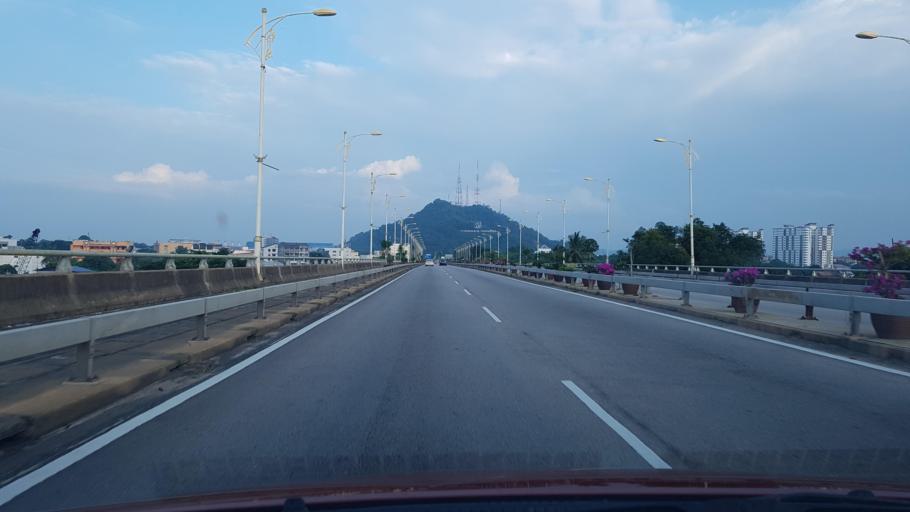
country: MY
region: Terengganu
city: Kuala Terengganu
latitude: 5.3224
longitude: 103.1258
